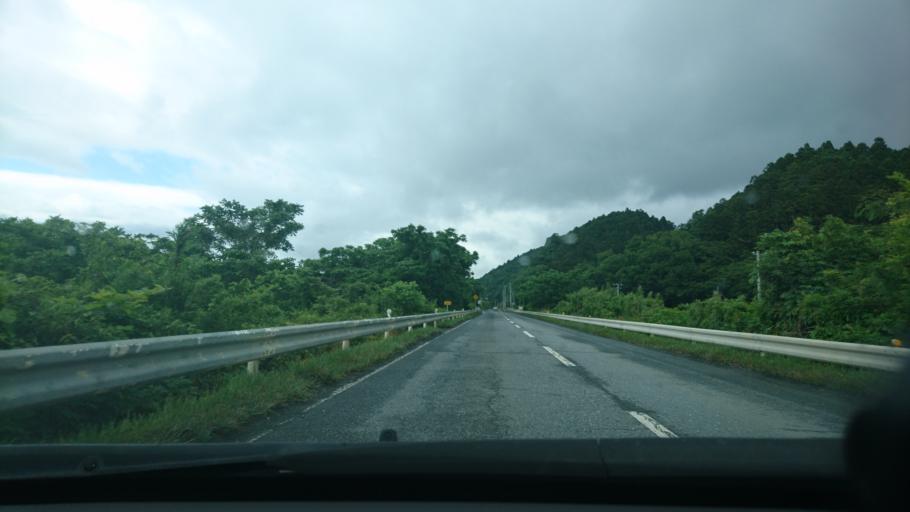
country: JP
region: Miyagi
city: Ishinomaki
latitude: 38.5639
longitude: 141.2997
